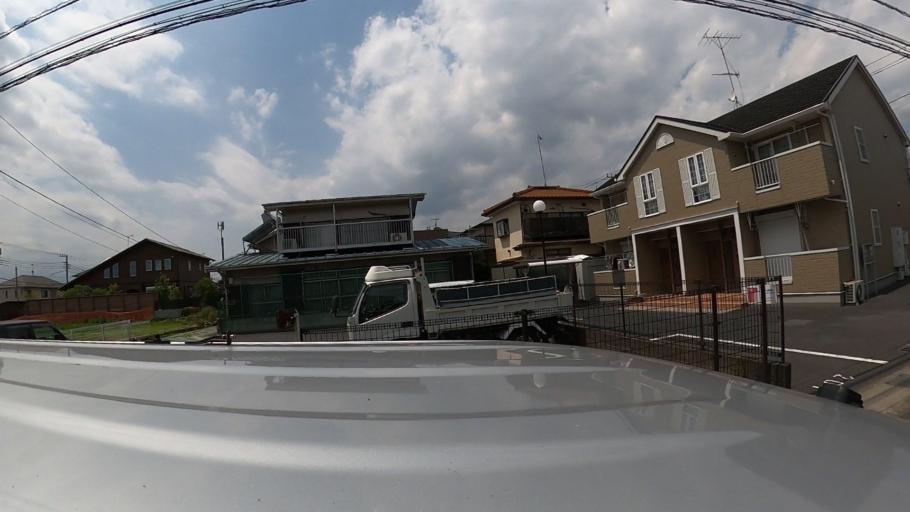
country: JP
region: Kanagawa
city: Chigasaki
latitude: 35.3899
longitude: 139.4034
